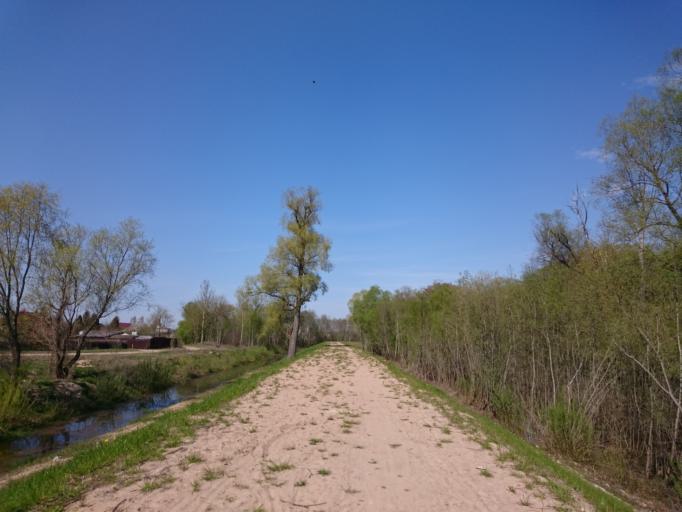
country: LV
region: Adazi
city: Adazi
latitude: 57.0906
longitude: 24.3226
